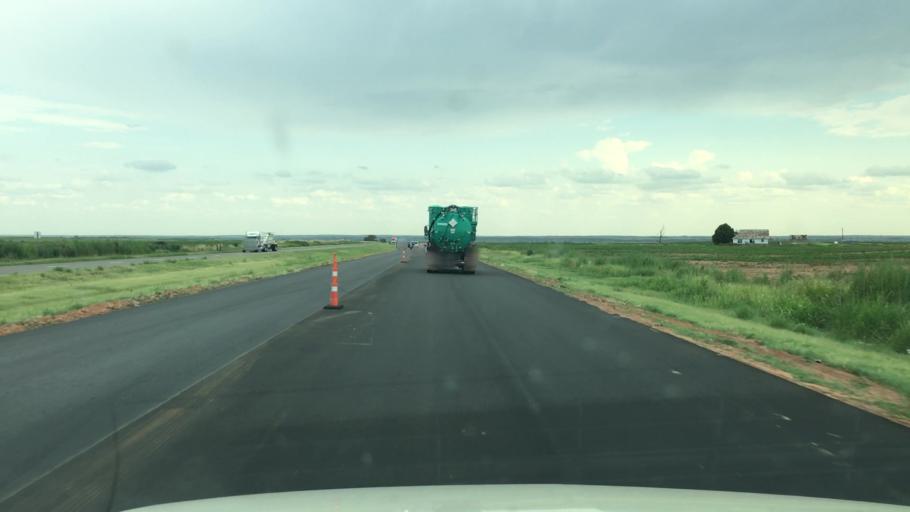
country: US
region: Texas
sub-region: Hall County
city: Memphis
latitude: 34.6176
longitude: -100.4712
